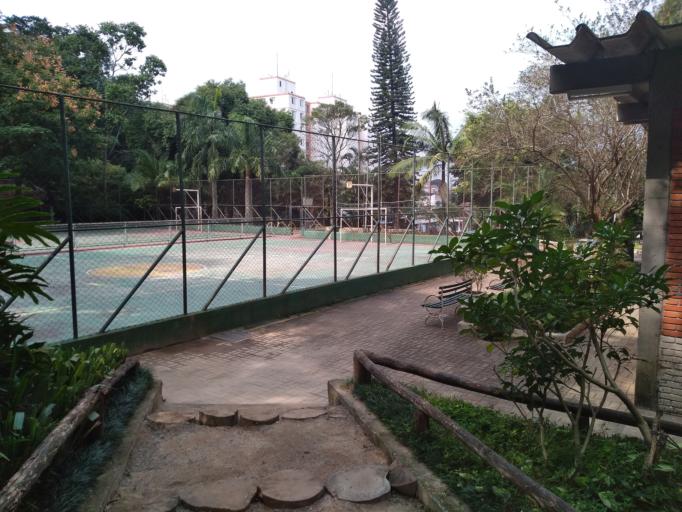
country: BR
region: Sao Paulo
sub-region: Taboao Da Serra
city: Taboao da Serra
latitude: -23.5839
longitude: -46.7300
